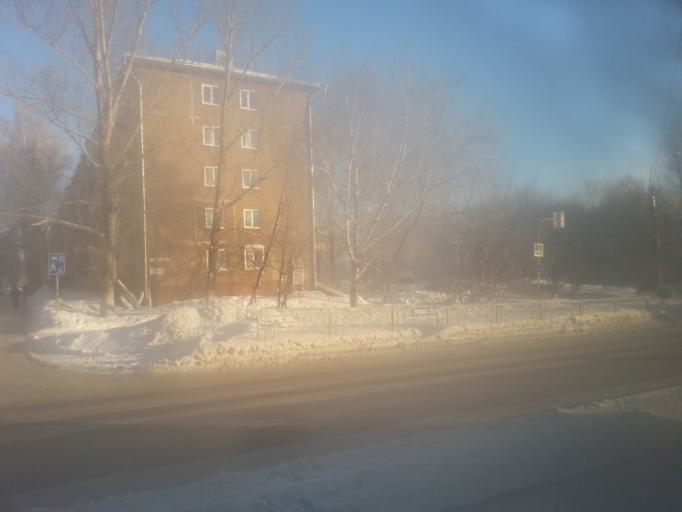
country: RU
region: Altai Krai
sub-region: Gorod Barnaulskiy
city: Barnaul
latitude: 53.3575
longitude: 83.7086
